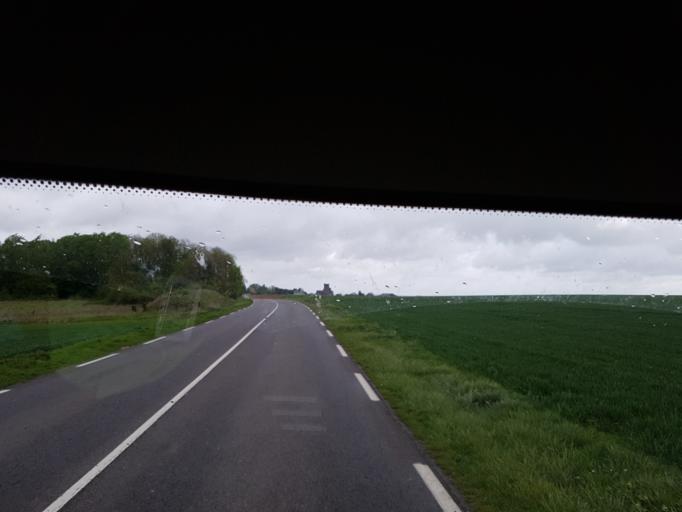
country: FR
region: Picardie
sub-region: Departement de l'Aisne
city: Crouy
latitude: 49.4370
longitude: 3.3554
